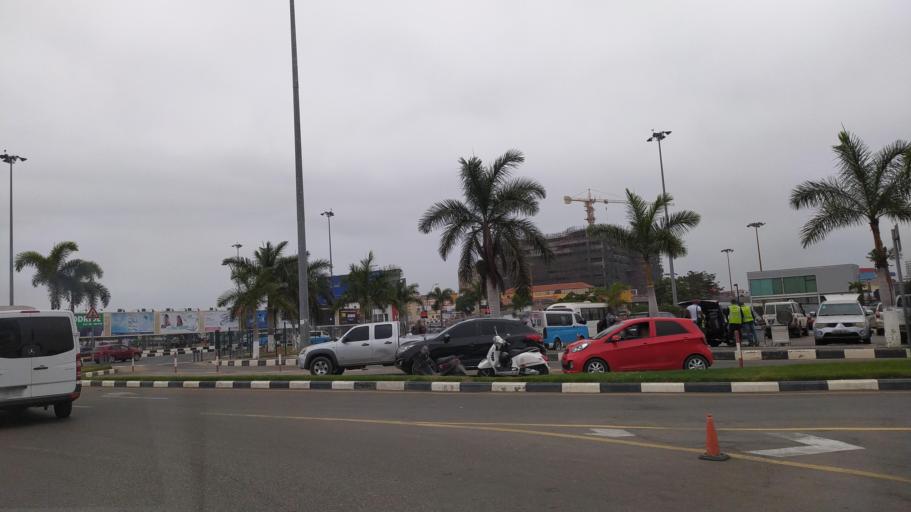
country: AO
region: Luanda
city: Luanda
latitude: -8.8469
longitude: 13.2353
